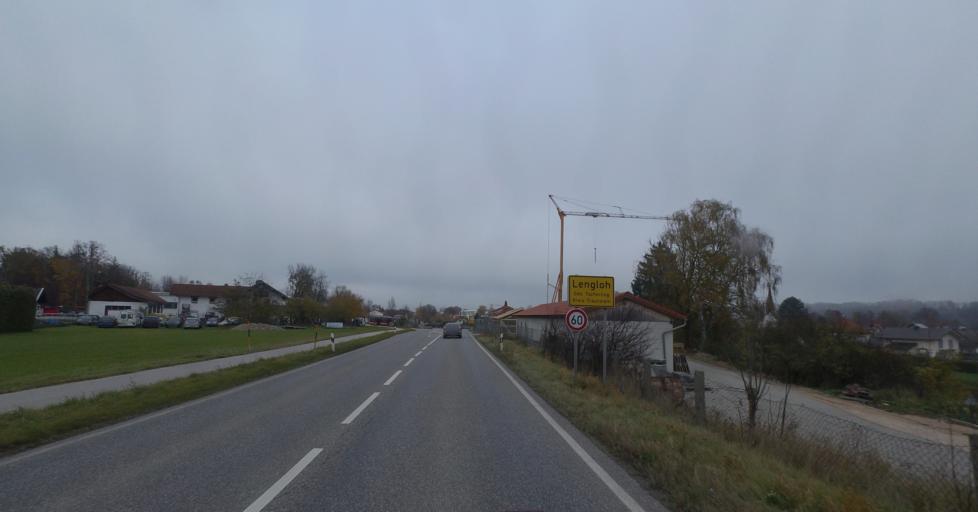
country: DE
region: Bavaria
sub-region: Upper Bavaria
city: Tacherting
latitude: 48.0546
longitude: 12.5691
